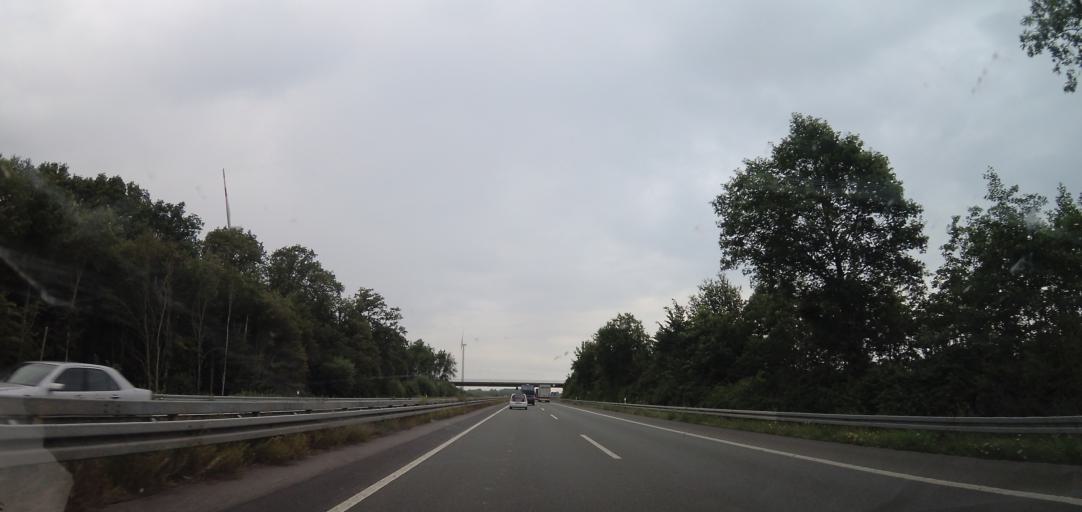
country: DE
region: North Rhine-Westphalia
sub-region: Regierungsbezirk Munster
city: Gescher
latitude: 51.9200
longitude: 7.0317
